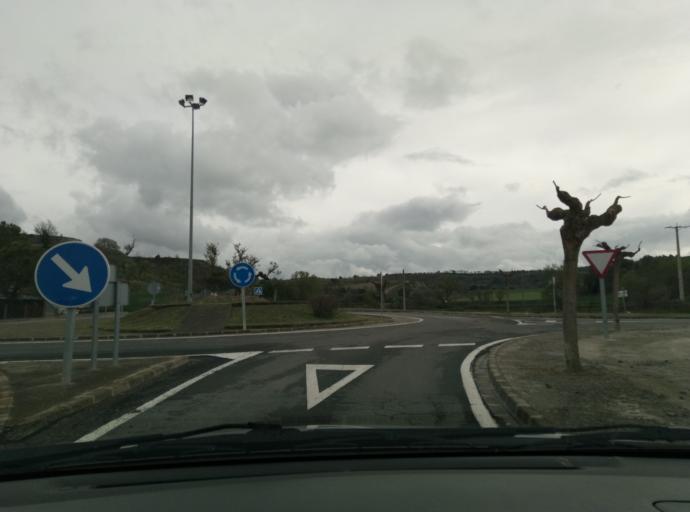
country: ES
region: Catalonia
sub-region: Provincia de Lleida
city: Cervera
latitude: 41.6260
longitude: 1.3396
